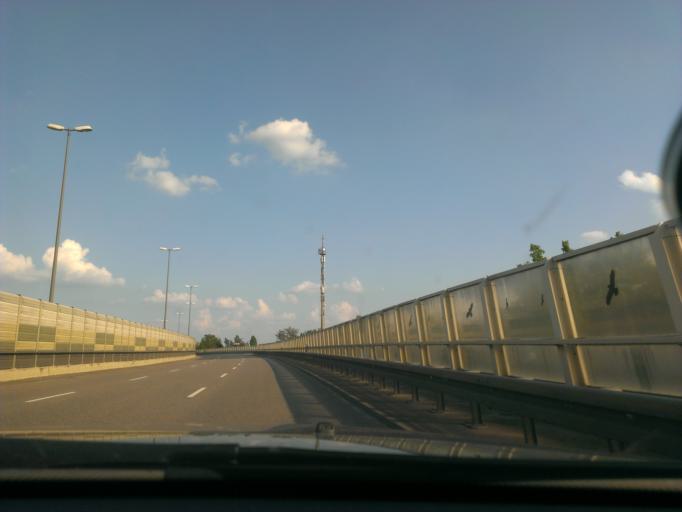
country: DE
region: Bavaria
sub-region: Regierungsbezirk Mittelfranken
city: Erlangen
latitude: 49.5906
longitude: 10.9964
